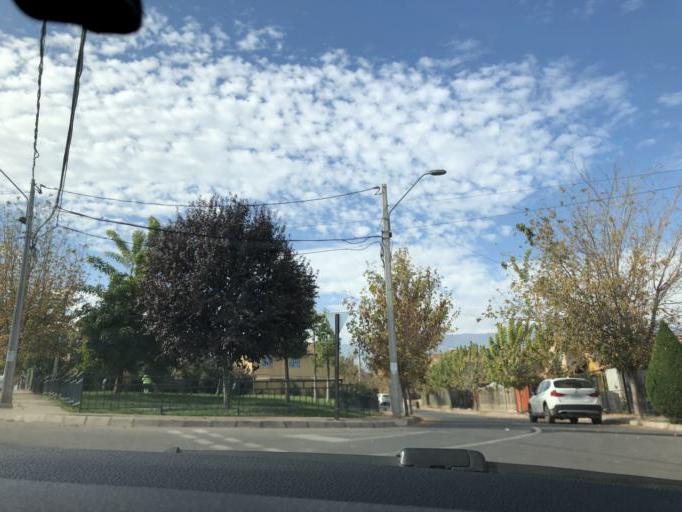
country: CL
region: Santiago Metropolitan
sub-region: Provincia de Cordillera
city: Puente Alto
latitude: -33.5881
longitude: -70.5335
